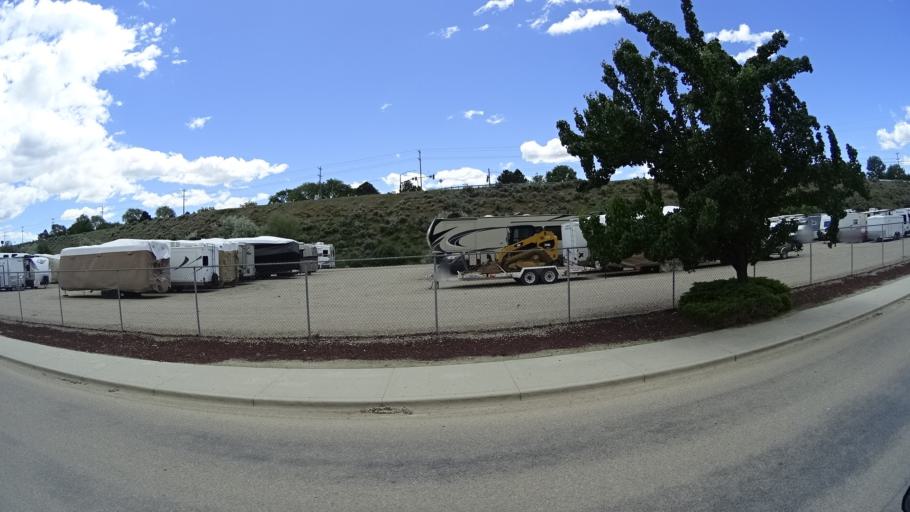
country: US
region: Idaho
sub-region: Ada County
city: Eagle
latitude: 43.6631
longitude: -116.3234
